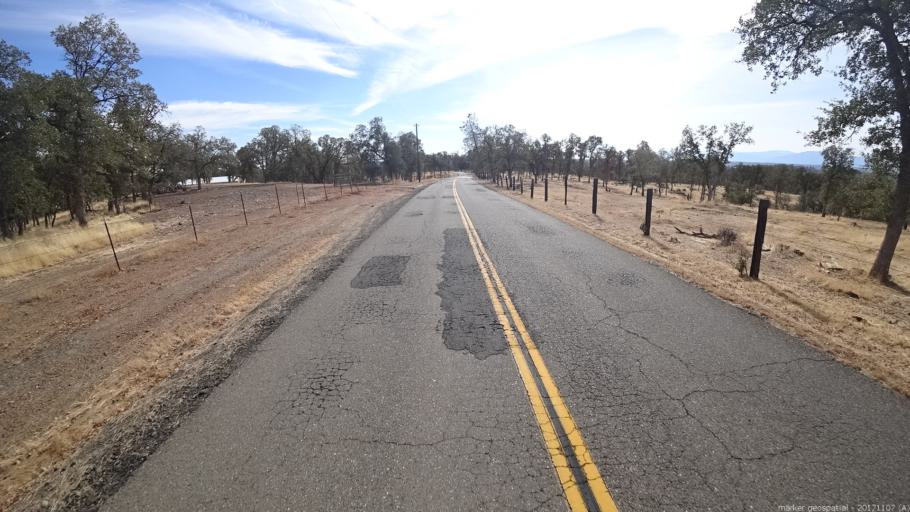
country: US
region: California
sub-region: Shasta County
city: Shasta
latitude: 40.4165
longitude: -122.5233
